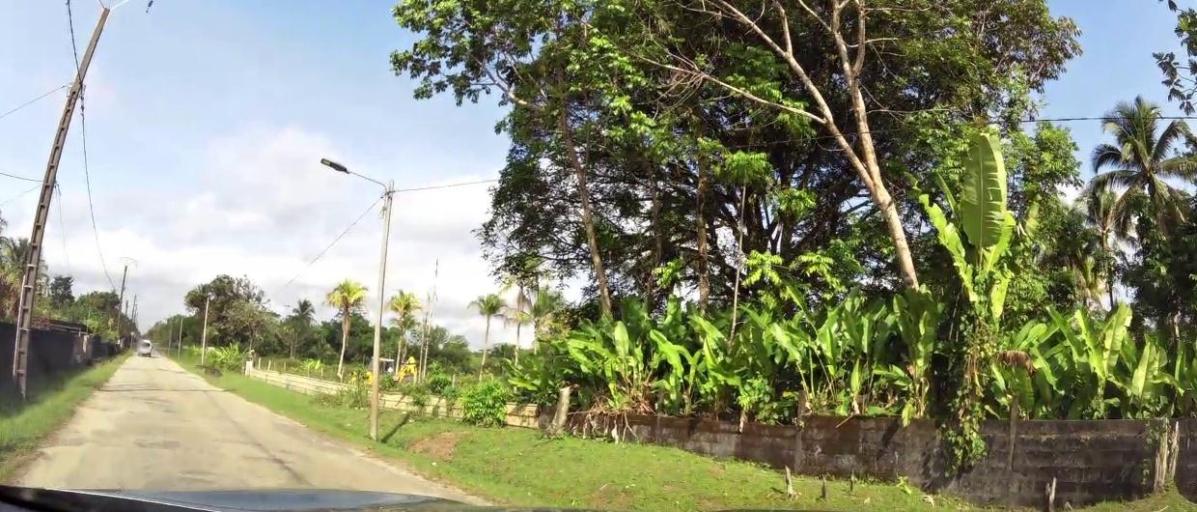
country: GF
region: Guyane
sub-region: Guyane
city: Roura
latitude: 4.7855
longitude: -52.3372
